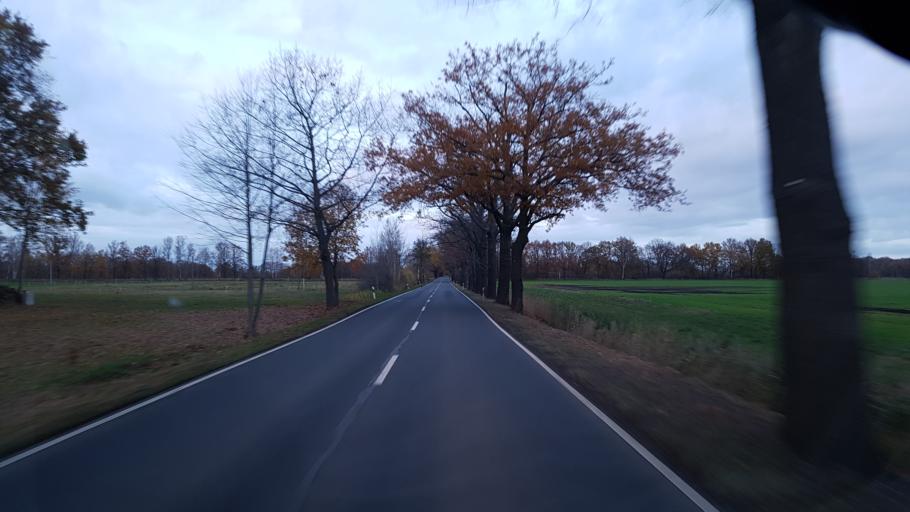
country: DE
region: Brandenburg
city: Schraden
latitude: 51.4504
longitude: 13.7111
